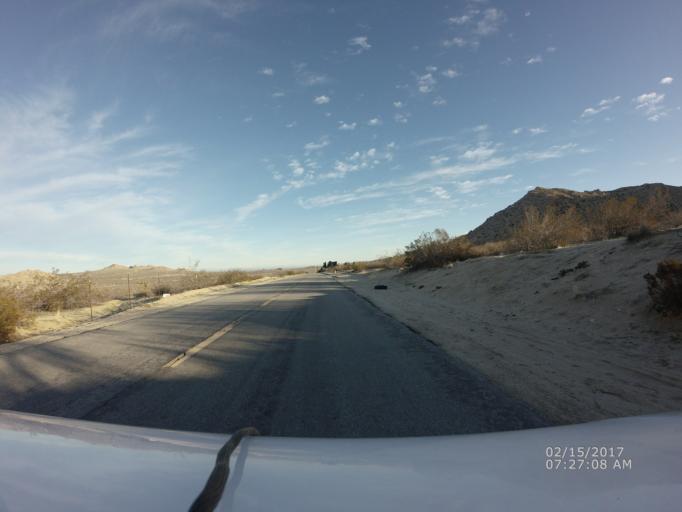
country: US
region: California
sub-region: Los Angeles County
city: Lake Los Angeles
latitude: 34.6026
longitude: -117.8713
